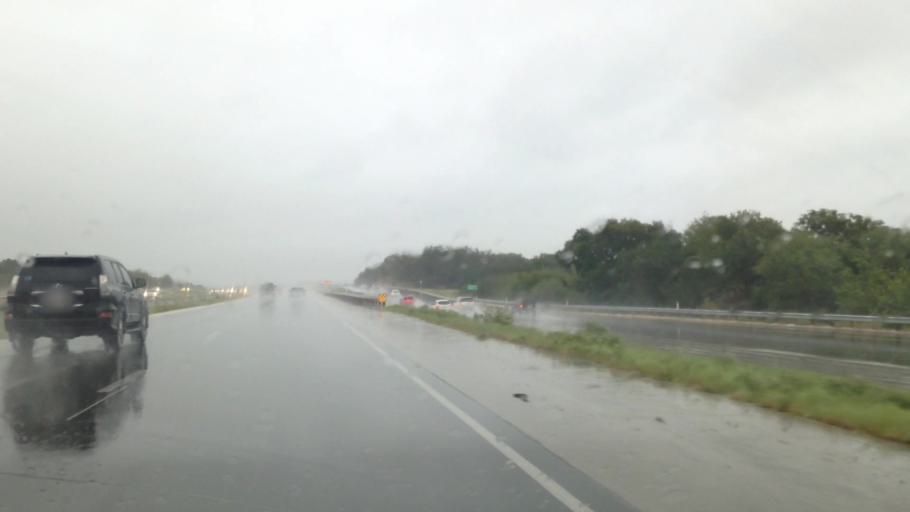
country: US
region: Texas
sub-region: Bexar County
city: Shavano Park
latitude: 29.6009
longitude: -98.5573
